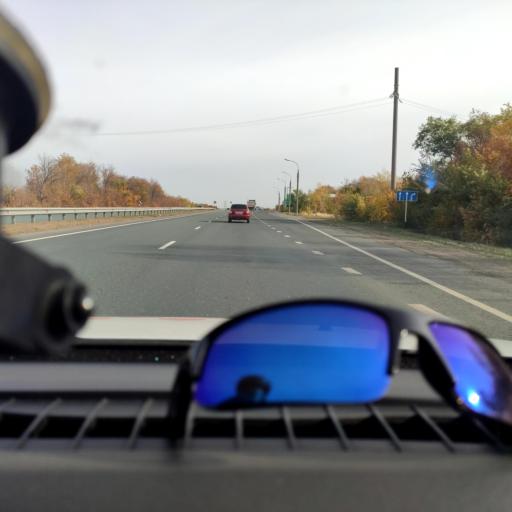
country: RU
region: Samara
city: Novokuybyshevsk
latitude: 53.0014
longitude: 49.9602
